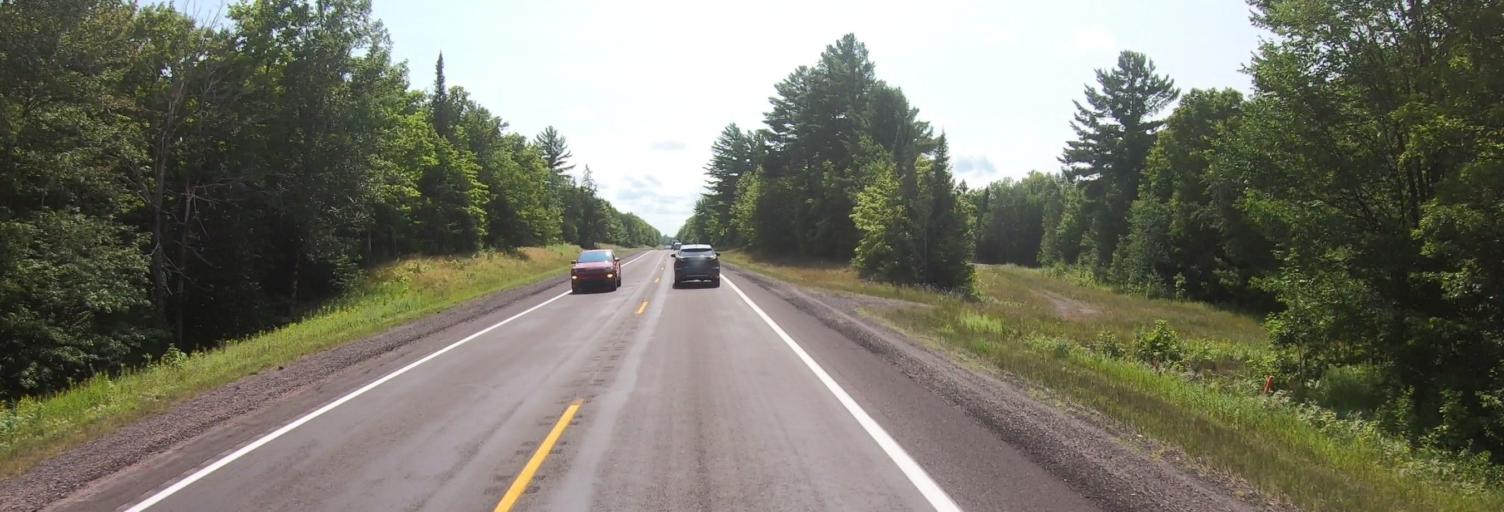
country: US
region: Michigan
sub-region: Houghton County
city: Hancock
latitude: 46.8691
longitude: -88.8981
